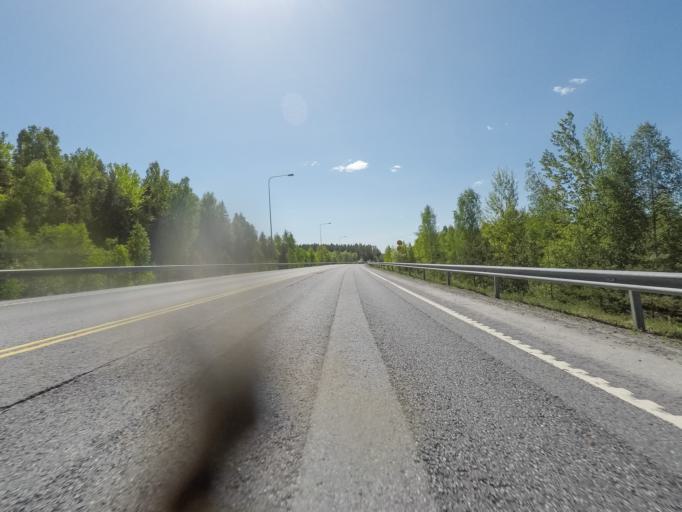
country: FI
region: Pirkanmaa
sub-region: Etelae-Pirkanmaa
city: Toijala
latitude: 61.1894
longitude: 23.8074
